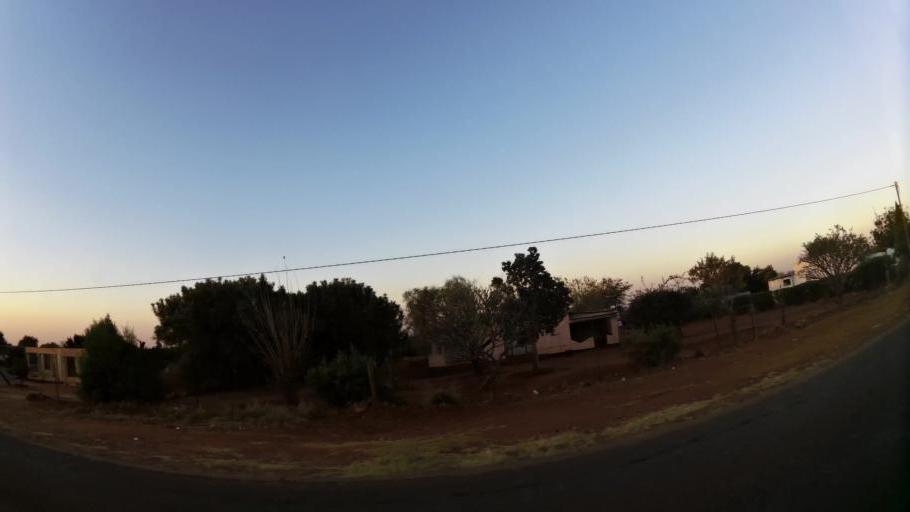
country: ZA
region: North-West
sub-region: Bojanala Platinum District Municipality
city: Rustenburg
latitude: -25.6134
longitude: 27.1915
